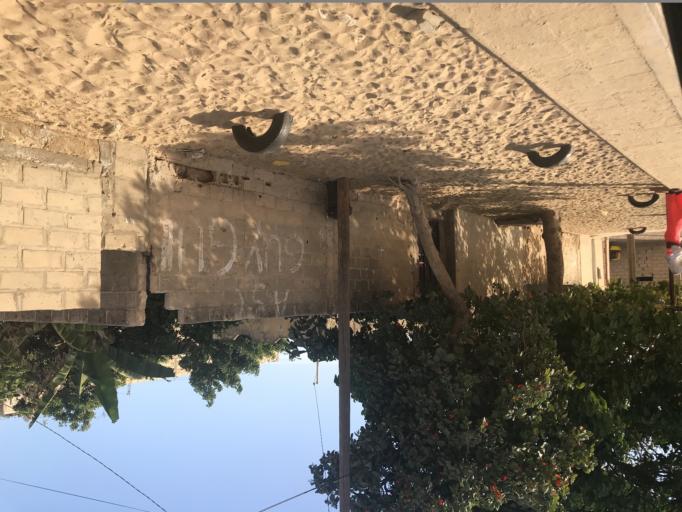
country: SN
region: Saint-Louis
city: Saint-Louis
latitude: 15.9934
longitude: -16.4914
